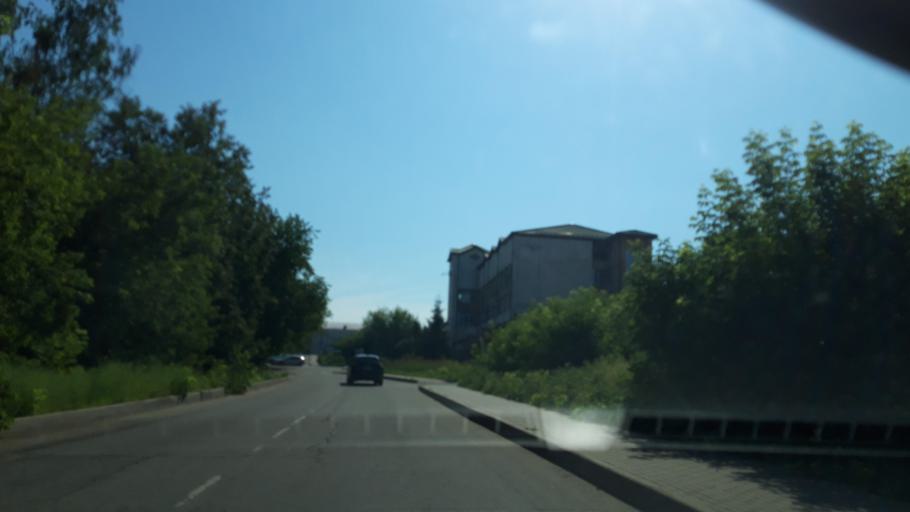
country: RU
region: Moskovskaya
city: Klin
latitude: 56.3331
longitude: 36.7343
